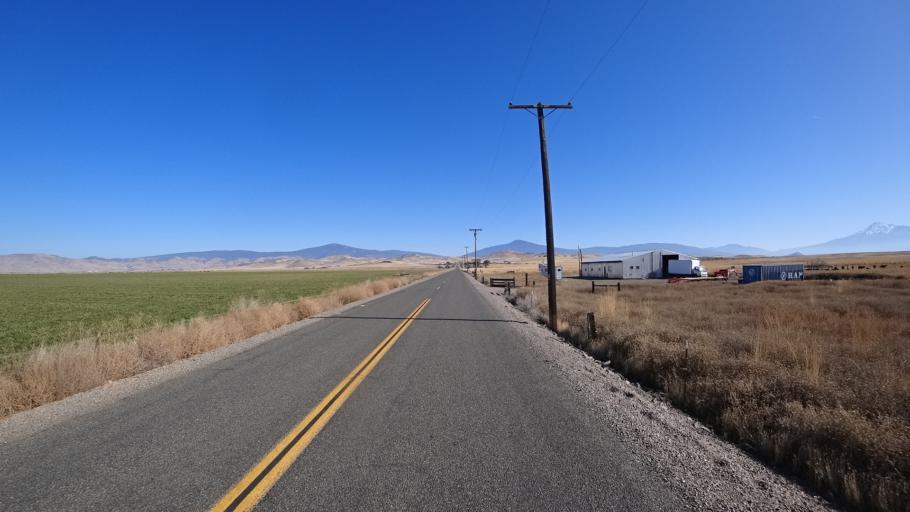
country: US
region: California
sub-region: Siskiyou County
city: Montague
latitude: 41.7561
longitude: -122.4855
